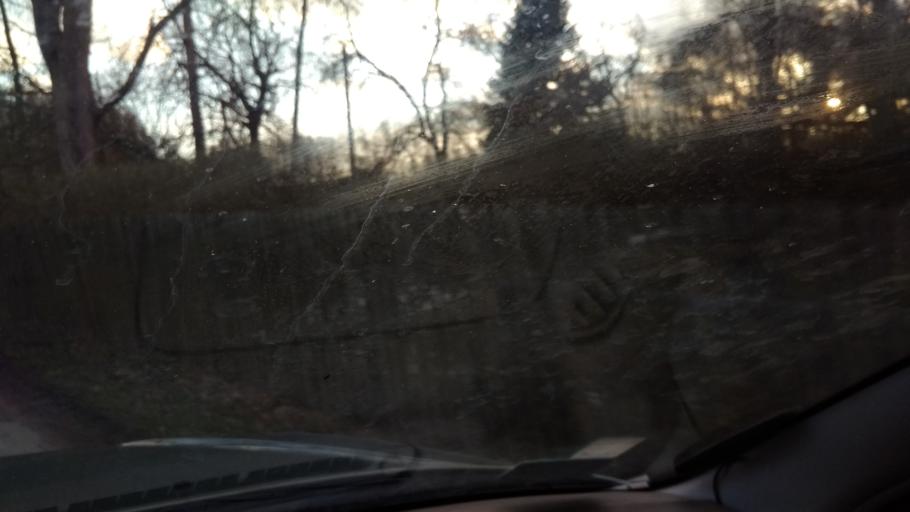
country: PL
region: Lower Silesian Voivodeship
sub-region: Powiat jeleniogorski
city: Sosnowka
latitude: 50.8429
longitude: 15.7389
